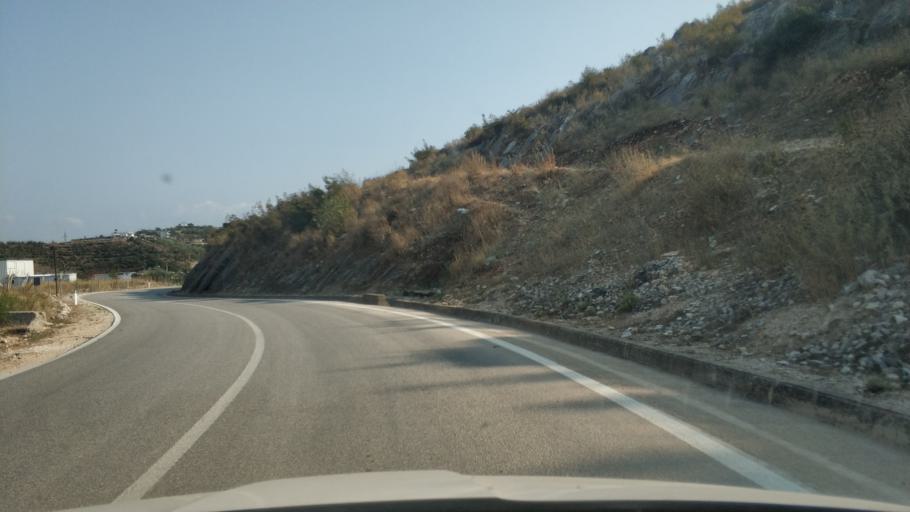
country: AL
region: Vlore
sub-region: Rrethi i Sarandes
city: Sarande
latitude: 39.8844
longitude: 20.0192
